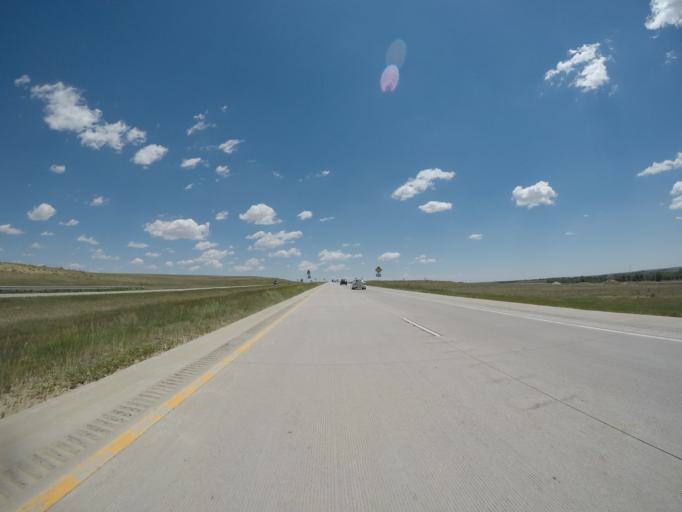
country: US
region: Colorado
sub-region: Lincoln County
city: Limon
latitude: 39.2732
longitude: -103.7243
